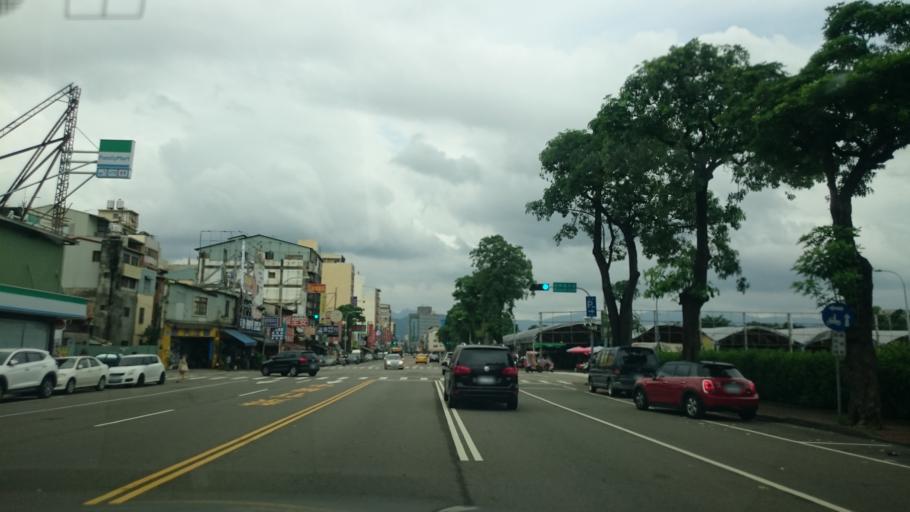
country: TW
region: Taiwan
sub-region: Taichung City
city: Taichung
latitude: 24.1429
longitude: 120.6888
